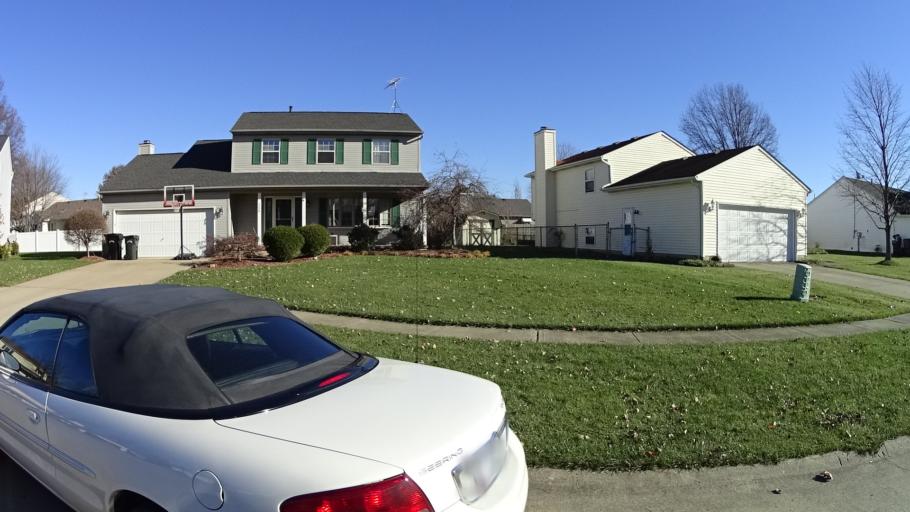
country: US
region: Ohio
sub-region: Lorain County
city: Elyria
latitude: 41.3512
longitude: -82.0808
